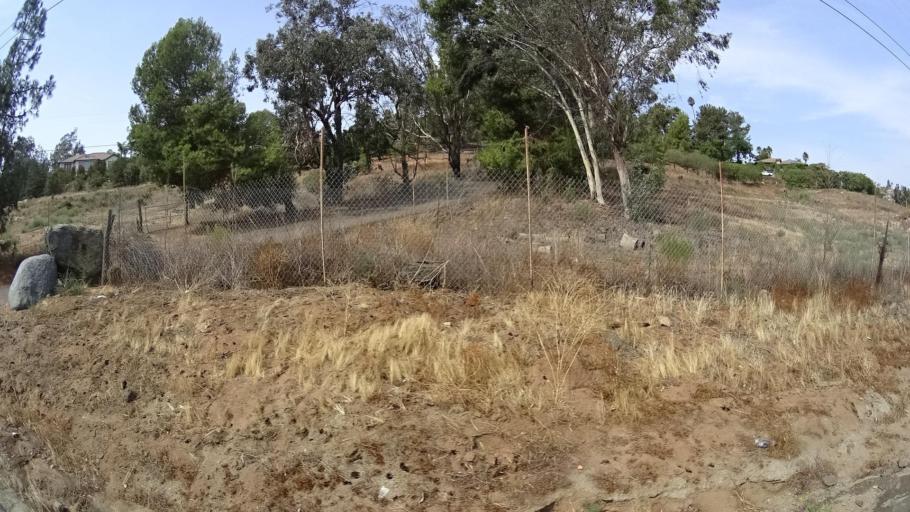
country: US
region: California
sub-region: San Diego County
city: Escondido
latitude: 33.0768
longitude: -117.0351
